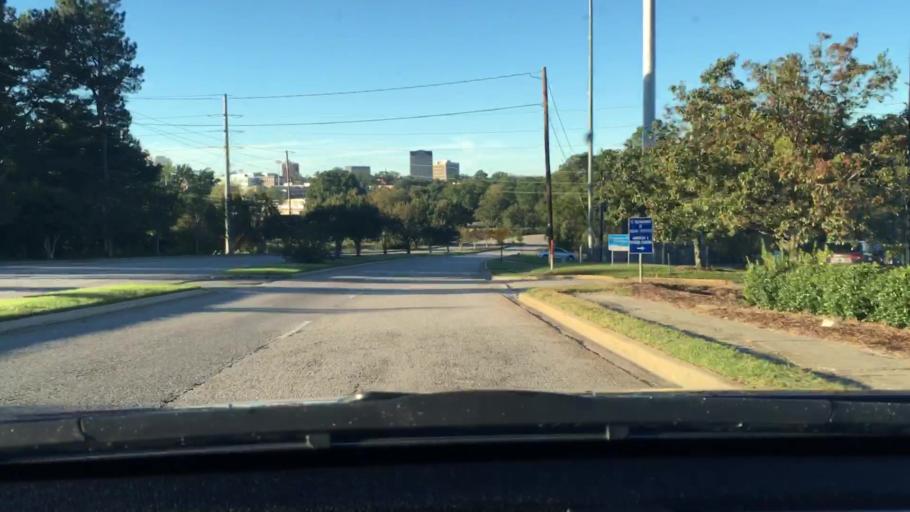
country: US
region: South Carolina
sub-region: Richland County
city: Columbia
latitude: 34.0250
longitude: -81.0286
